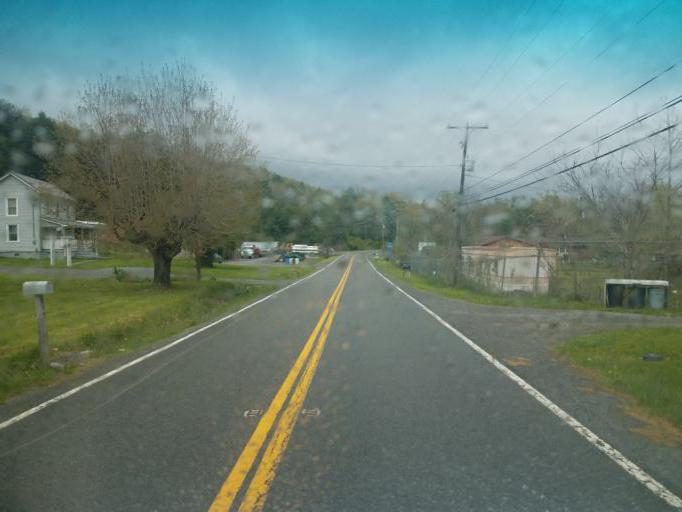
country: US
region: Virginia
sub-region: Bland County
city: Bland
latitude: 37.1587
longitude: -81.1497
